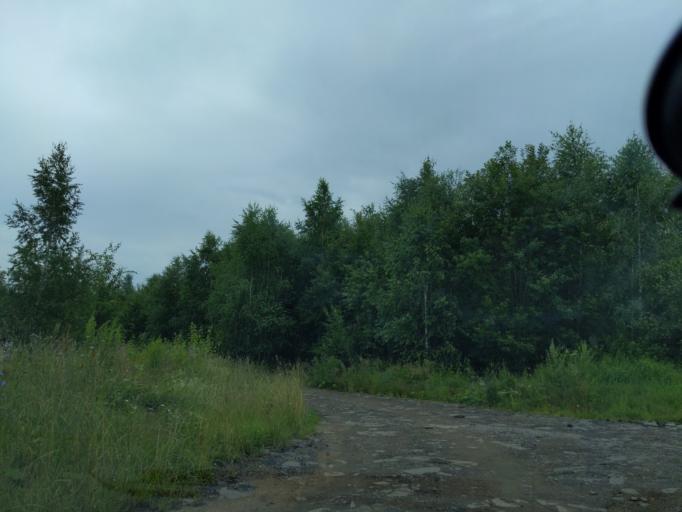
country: RU
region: Moskovskaya
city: Lugovaya
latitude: 56.0557
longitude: 37.4980
